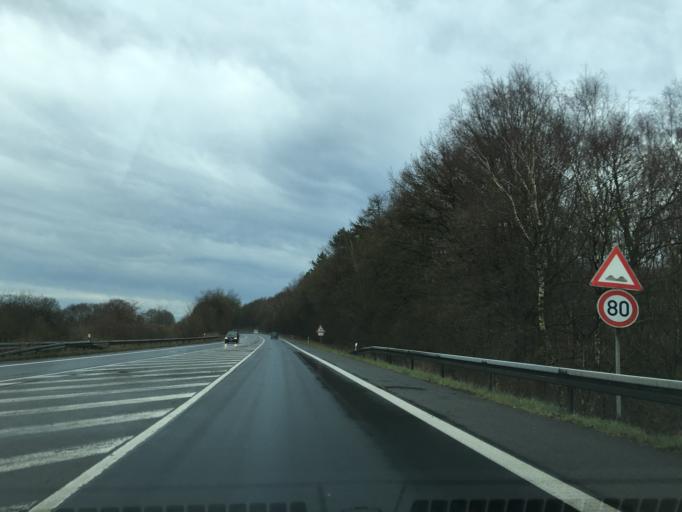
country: DE
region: North Rhine-Westphalia
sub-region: Regierungsbezirk Munster
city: Haltern
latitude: 51.7107
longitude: 7.1600
